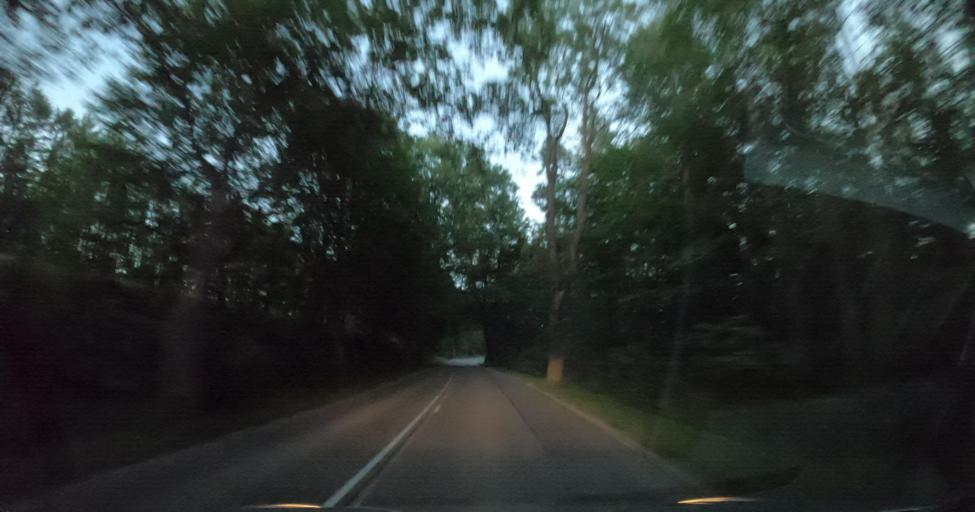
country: PL
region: Pomeranian Voivodeship
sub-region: Powiat wejherowski
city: Koleczkowo
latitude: 54.4692
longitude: 18.2990
